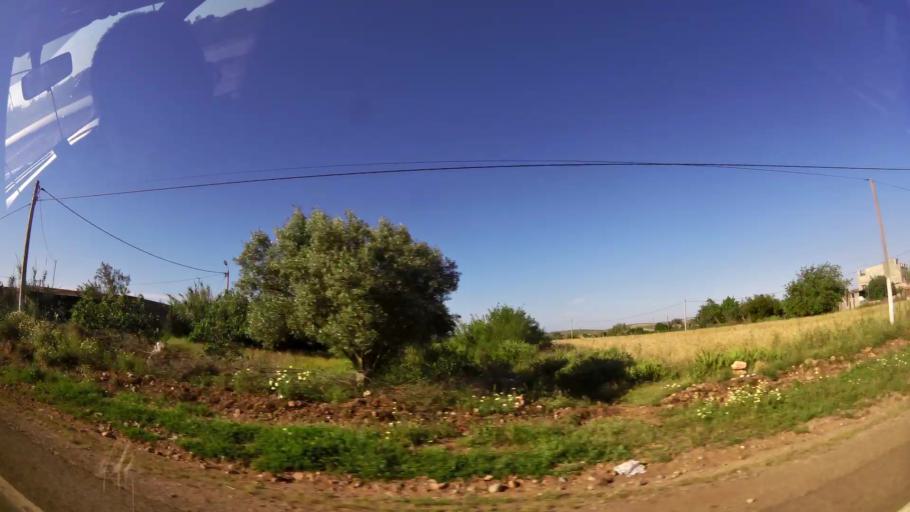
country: MA
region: Oriental
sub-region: Berkane-Taourirt
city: Ahfir
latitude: 35.0045
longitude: -2.1831
